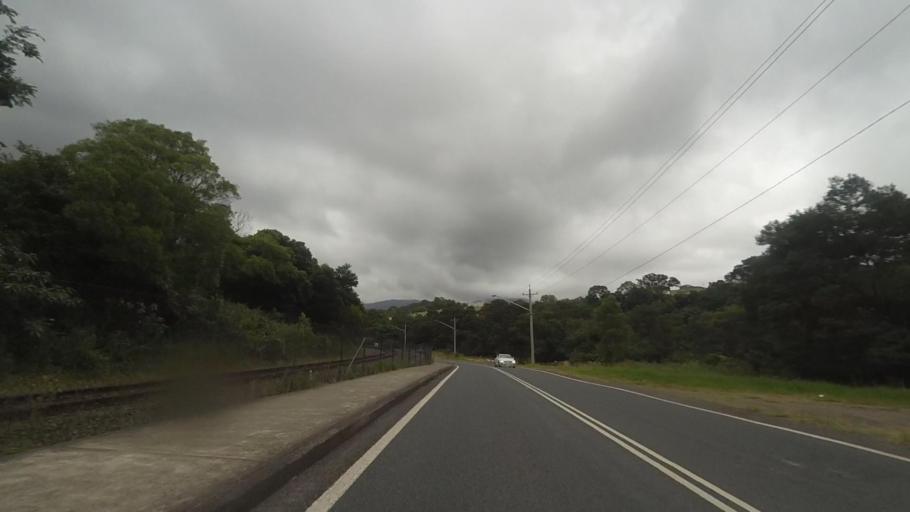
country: AU
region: New South Wales
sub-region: Wollongong
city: Cordeaux Heights
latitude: -34.4420
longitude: 150.8418
